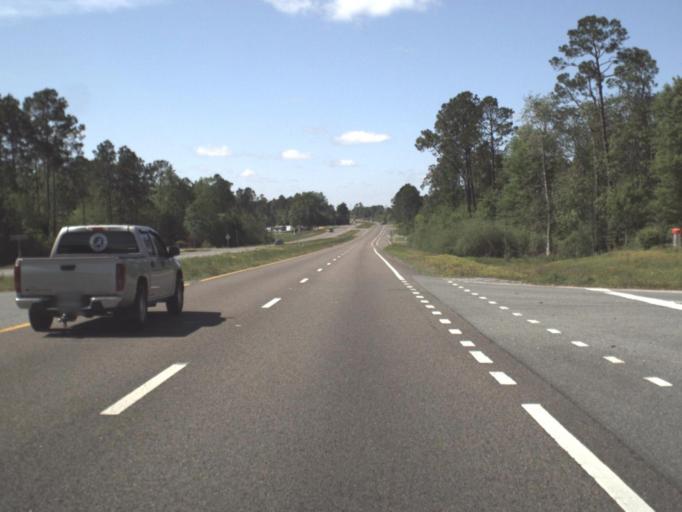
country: US
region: Florida
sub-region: Escambia County
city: Cantonment
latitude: 30.6175
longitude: -87.3242
